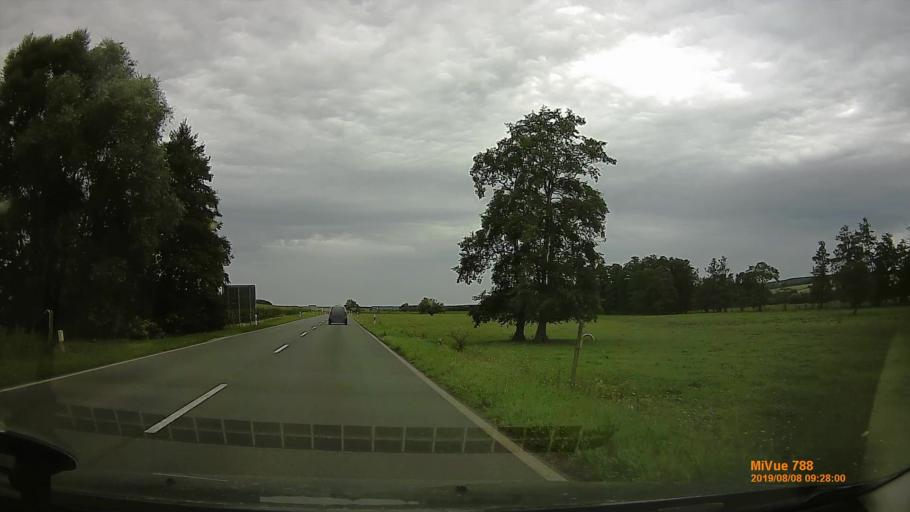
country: HU
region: Vas
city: Vasvar
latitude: 46.9569
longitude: 16.8460
